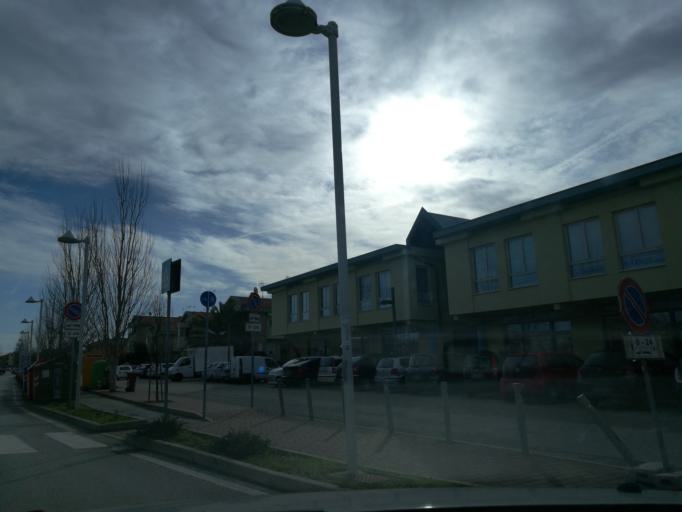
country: IT
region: The Marches
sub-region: Provincia di Pesaro e Urbino
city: Marotta
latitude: 43.7741
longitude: 13.1245
